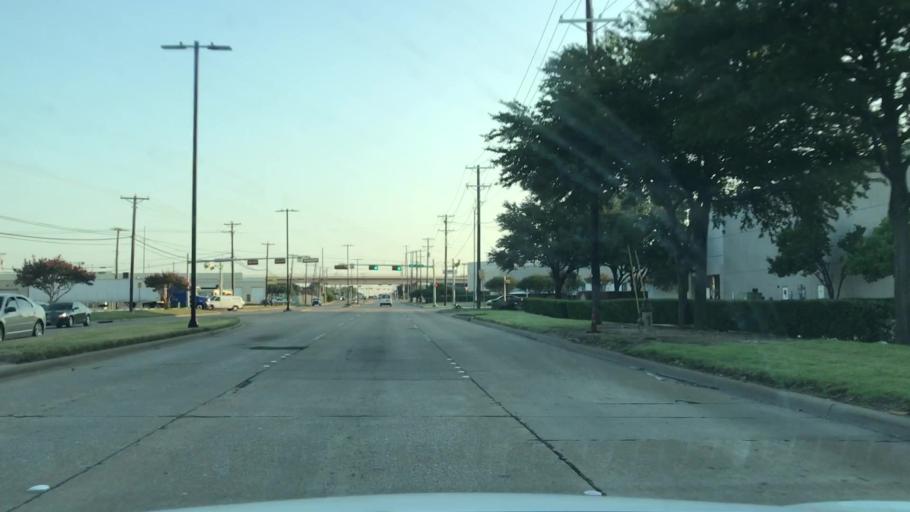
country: US
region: Texas
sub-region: Dallas County
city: Garland
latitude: 32.9038
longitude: -96.6828
